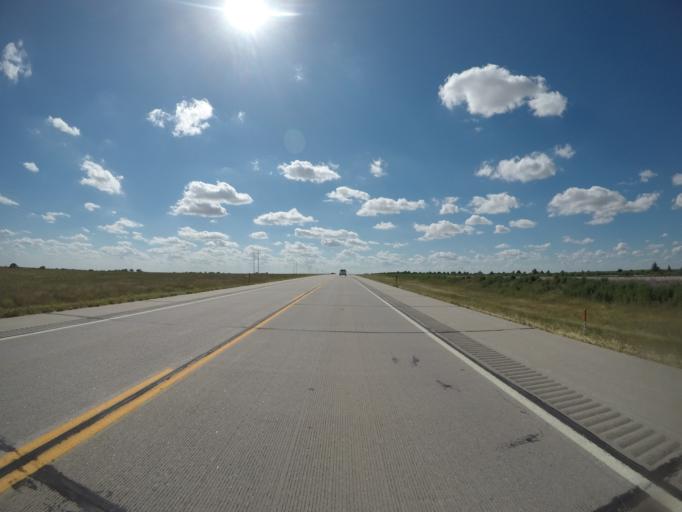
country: US
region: Colorado
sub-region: Phillips County
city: Holyoke
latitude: 40.5971
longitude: -102.3805
